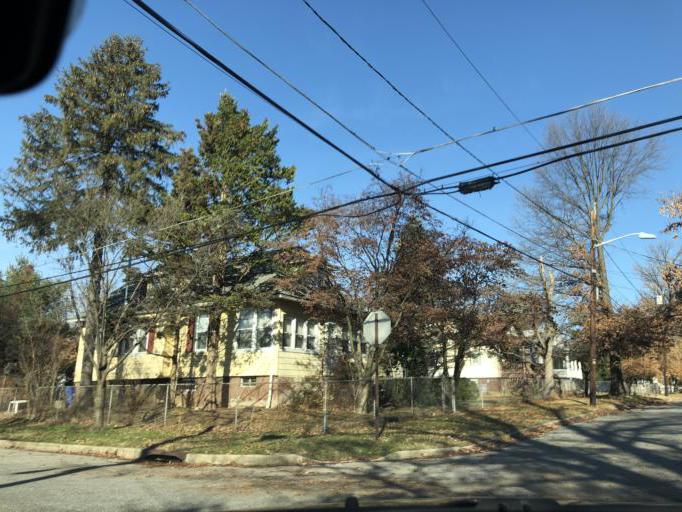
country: US
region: New Jersey
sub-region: Burlington County
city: Moorestown-Lenola
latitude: 39.9636
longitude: -74.9796
